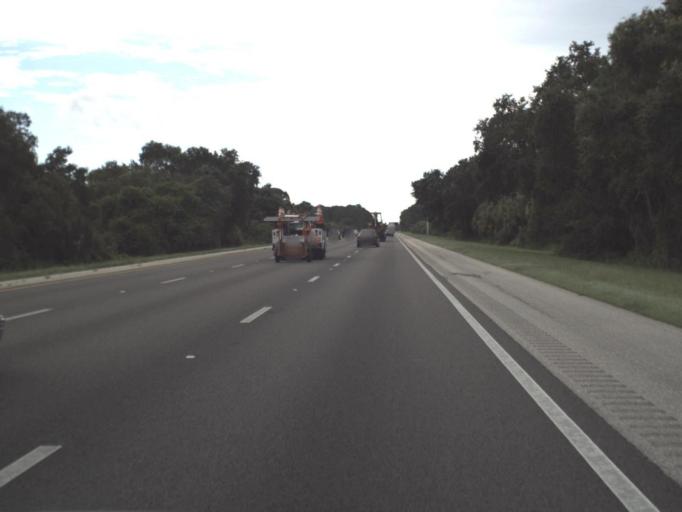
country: US
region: Florida
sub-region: Sarasota County
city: Vamo
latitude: 27.2229
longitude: -82.4503
